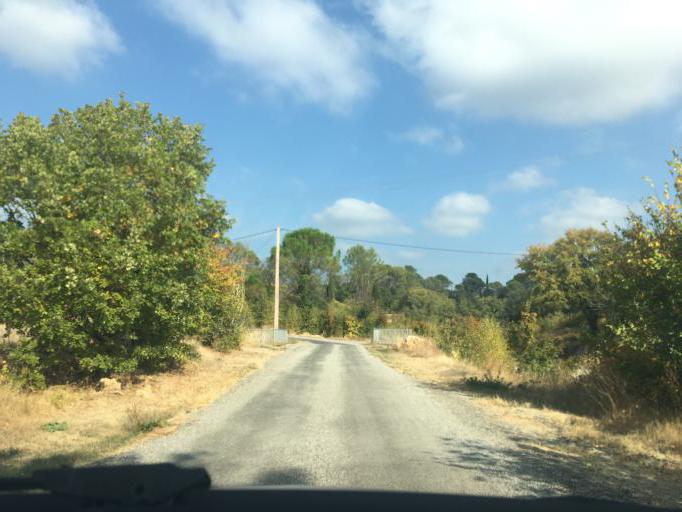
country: FR
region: Provence-Alpes-Cote d'Azur
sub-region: Departement du Var
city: Lorgues
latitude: 43.4866
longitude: 6.3998
